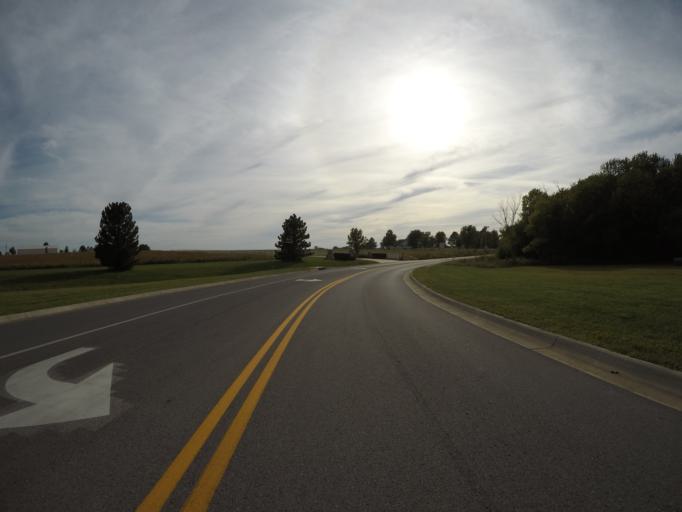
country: US
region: Kansas
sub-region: Douglas County
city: Baldwin City
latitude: 38.7751
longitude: -95.1670
